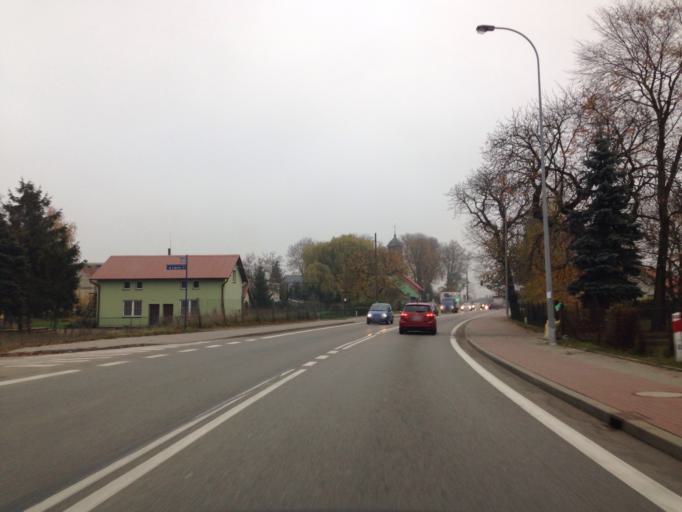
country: PL
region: Pomeranian Voivodeship
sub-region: Powiat gdanski
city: Legowo
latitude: 54.2038
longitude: 18.6646
